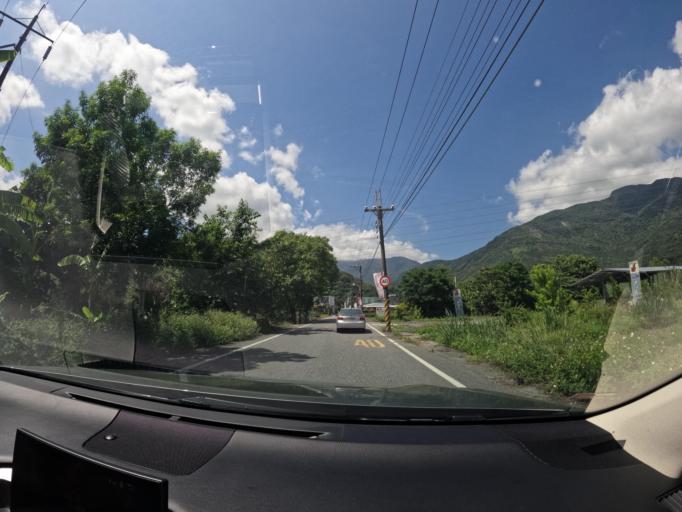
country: TW
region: Taiwan
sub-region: Hualien
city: Hualian
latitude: 23.7140
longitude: 121.4156
